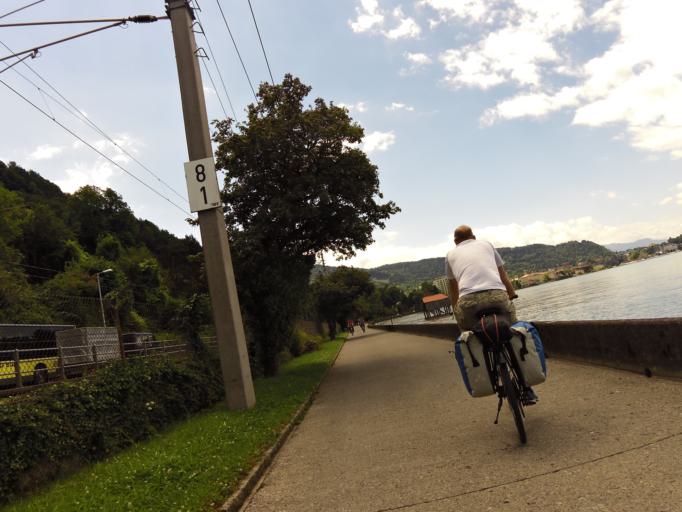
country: AT
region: Vorarlberg
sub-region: Politischer Bezirk Bregenz
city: Lochau
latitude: 47.5188
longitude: 9.7527
